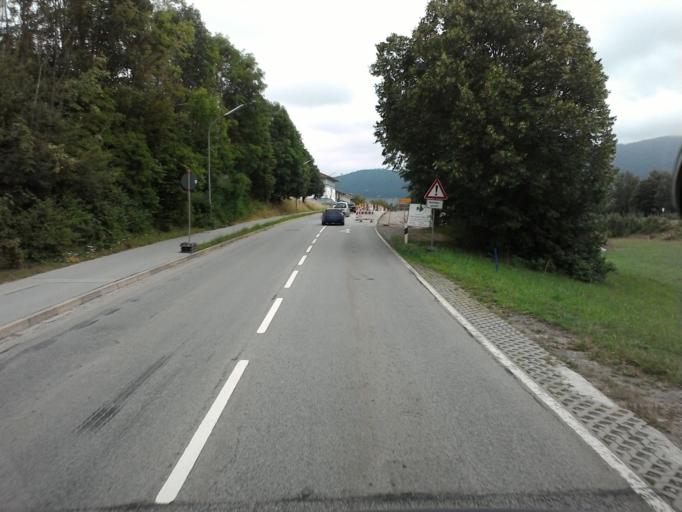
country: DE
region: Bavaria
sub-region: Upper Bavaria
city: Hausham
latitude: 47.7642
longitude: 11.8264
